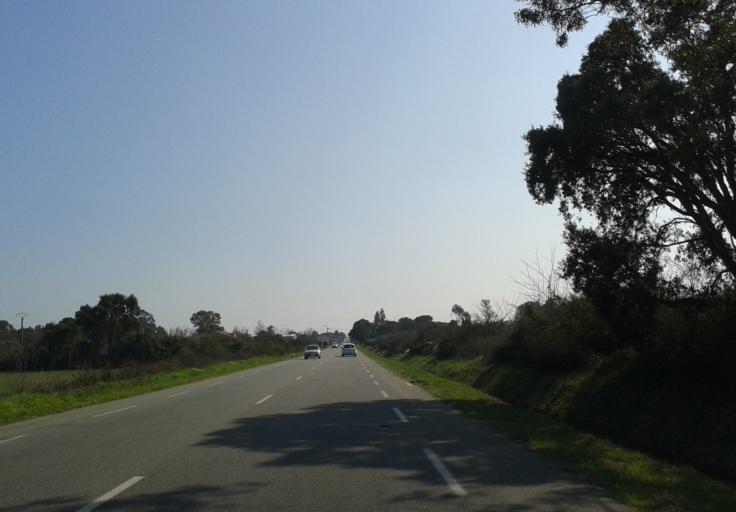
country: FR
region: Corsica
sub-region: Departement de la Haute-Corse
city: San-Nicolao
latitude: 42.3332
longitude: 9.5367
